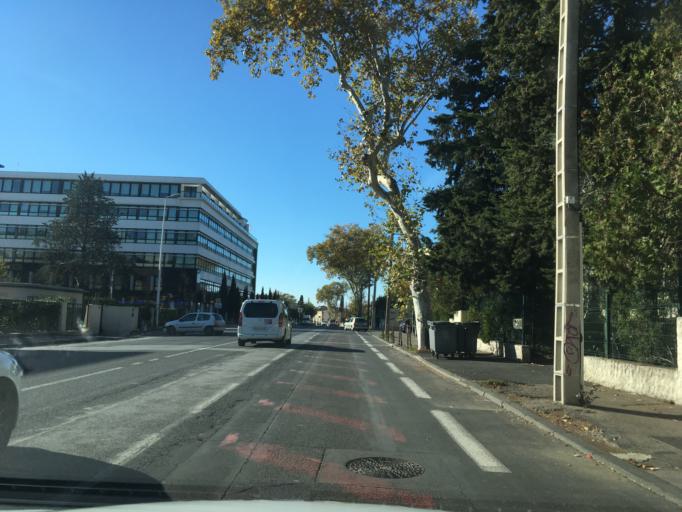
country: FR
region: Languedoc-Roussillon
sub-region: Departement de l'Herault
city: Juvignac
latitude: 43.6148
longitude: 3.8338
